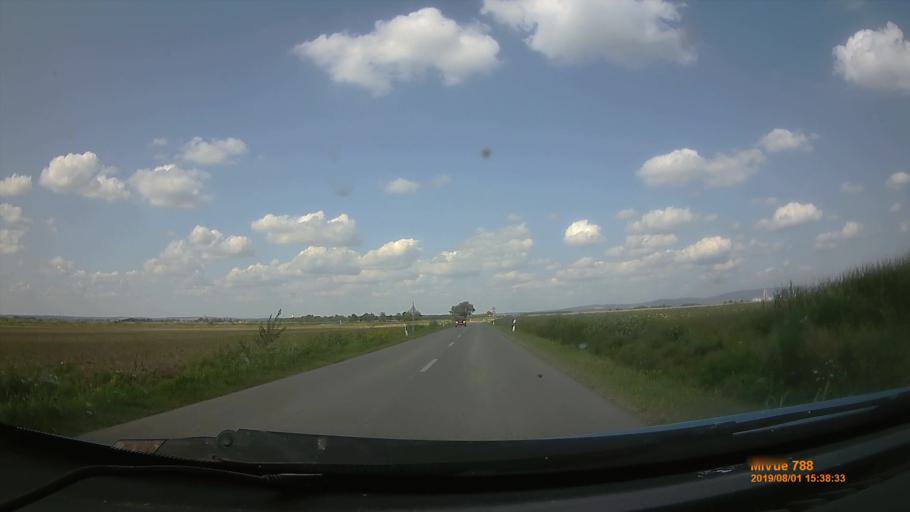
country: HU
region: Baranya
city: Szentlorinc
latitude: 45.9870
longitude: 17.9278
